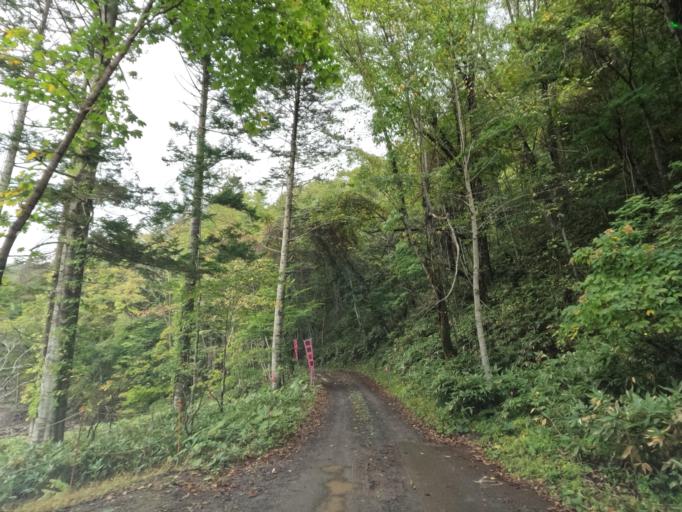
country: JP
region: Hokkaido
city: Date
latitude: 42.4969
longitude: 140.9327
